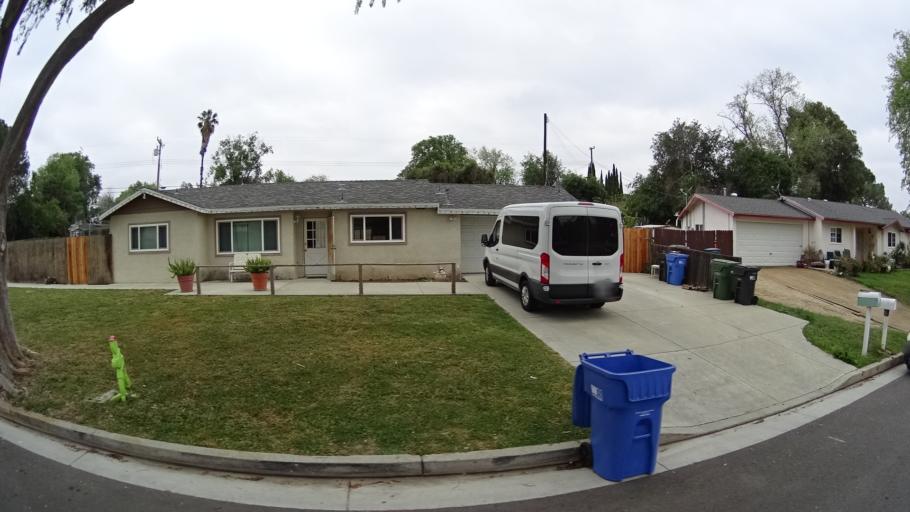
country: US
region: California
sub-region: Ventura County
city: Thousand Oaks
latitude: 34.2079
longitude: -118.8539
